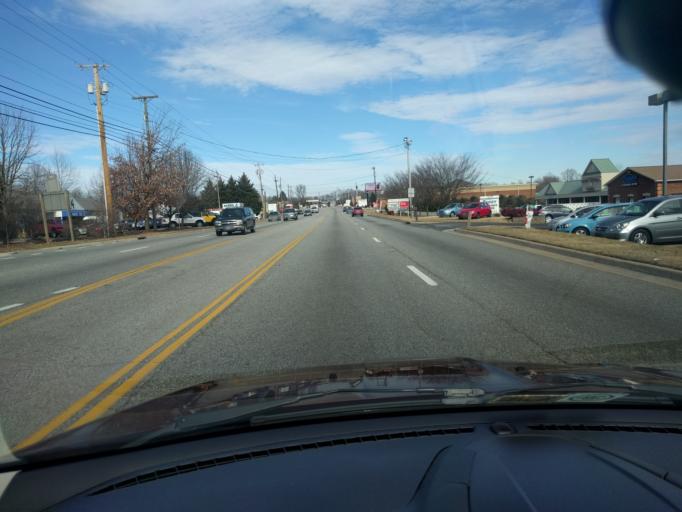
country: US
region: Virginia
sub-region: Bedford County
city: Forest
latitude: 37.3795
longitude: -79.2478
